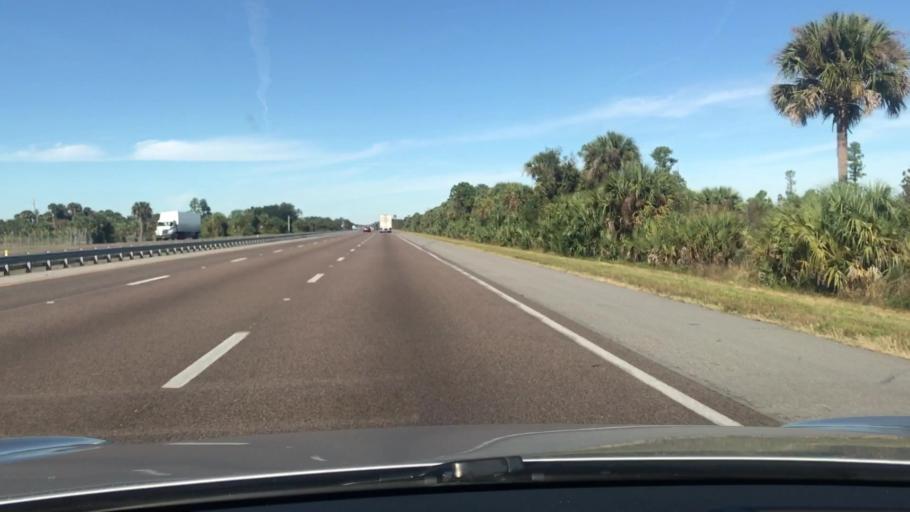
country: US
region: Florida
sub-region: Volusia County
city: Oak Hill
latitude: 28.8011
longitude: -80.9021
